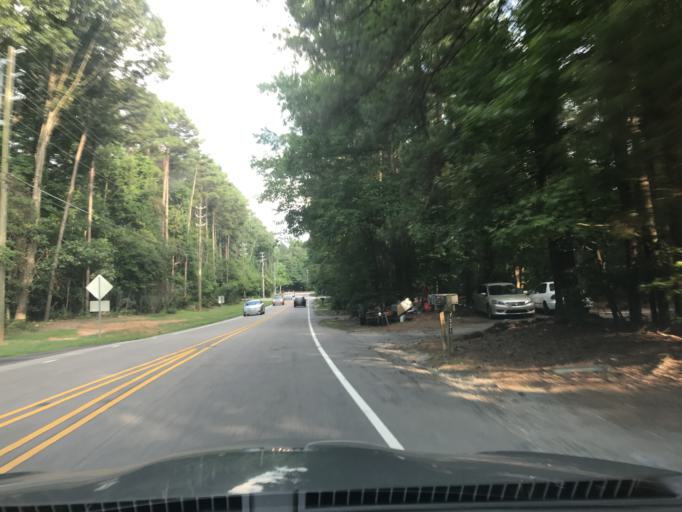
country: US
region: North Carolina
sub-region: Wake County
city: West Raleigh
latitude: 35.8773
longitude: -78.7040
